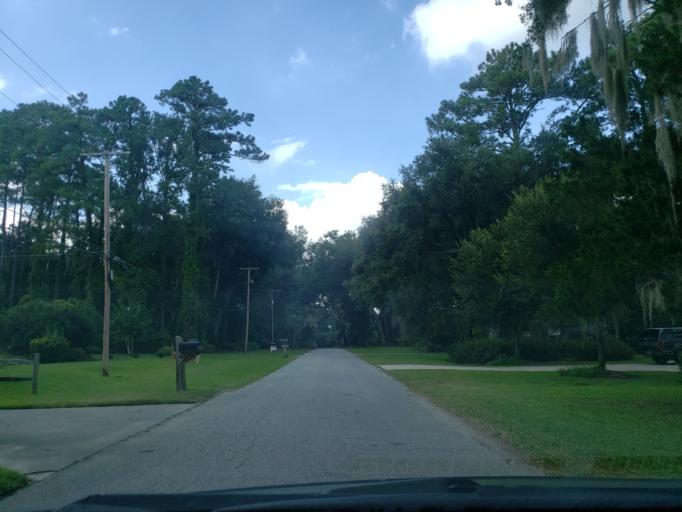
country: US
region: Georgia
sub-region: Chatham County
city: Montgomery
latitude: 31.9289
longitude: -81.0980
